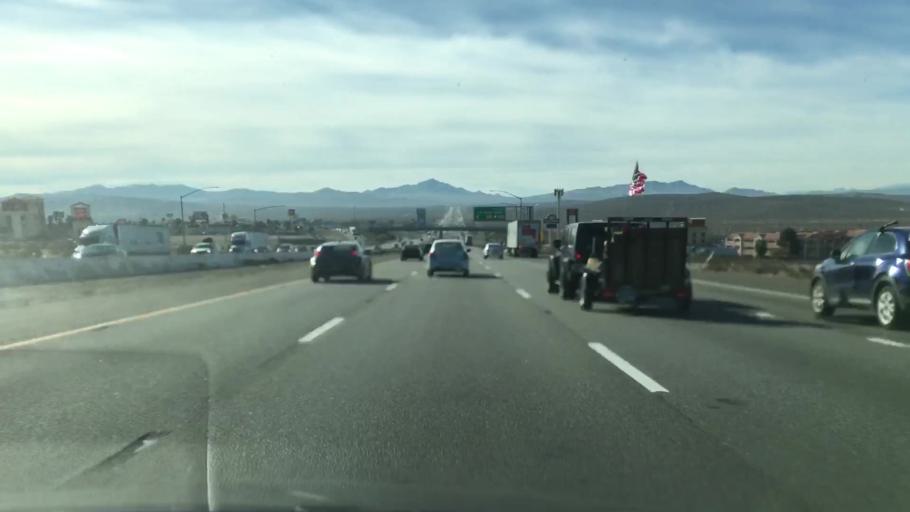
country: US
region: California
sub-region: San Bernardino County
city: Lenwood
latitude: 34.8593
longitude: -117.0835
